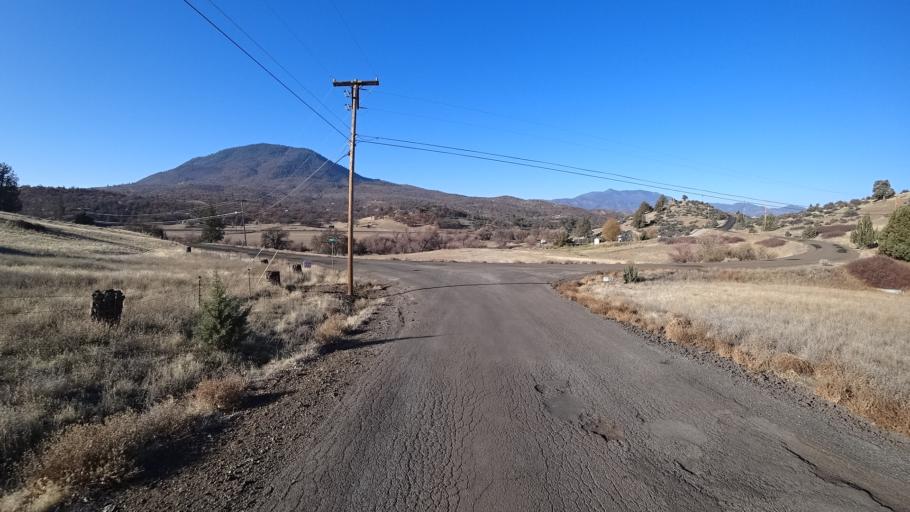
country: US
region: California
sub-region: Siskiyou County
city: Montague
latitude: 41.8930
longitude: -122.4802
